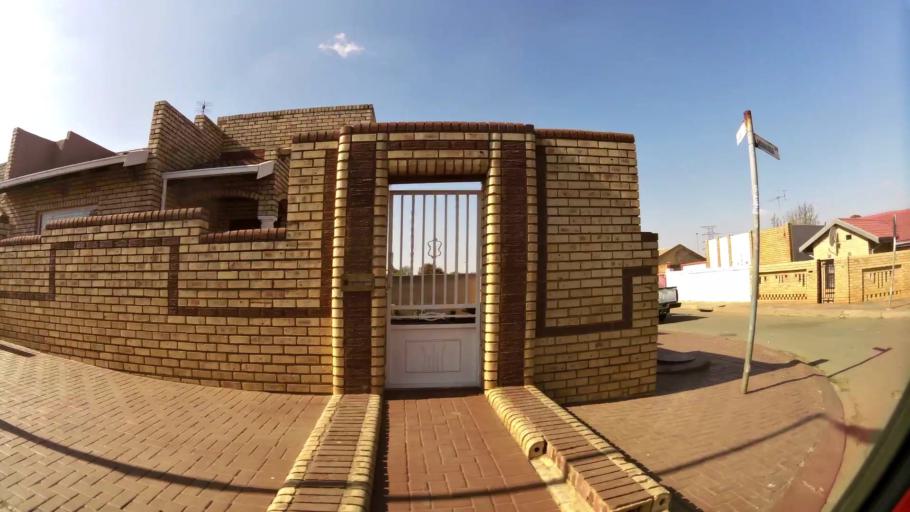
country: ZA
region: Gauteng
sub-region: City of Johannesburg Metropolitan Municipality
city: Soweto
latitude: -26.2379
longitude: 27.8793
